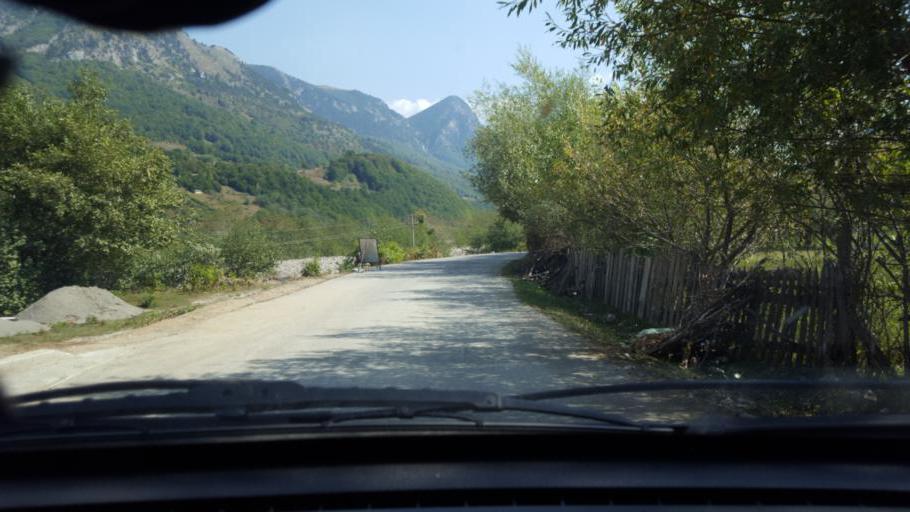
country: ME
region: Andrijevica
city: Andrijevica
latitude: 42.5897
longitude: 19.6939
